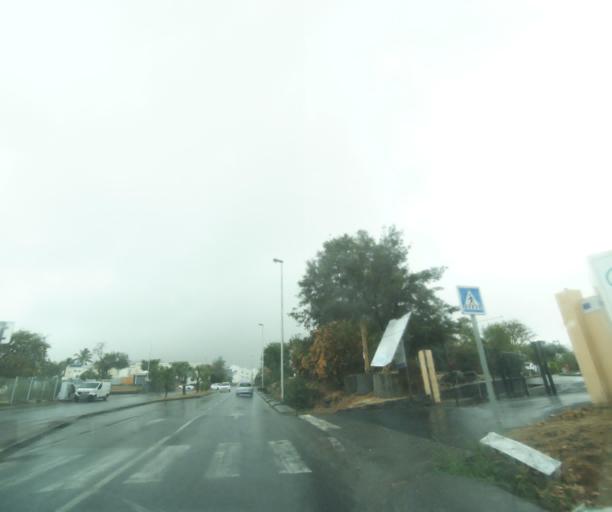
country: RE
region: Reunion
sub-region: Reunion
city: Saint-Paul
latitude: -21.0204
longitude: 55.2656
